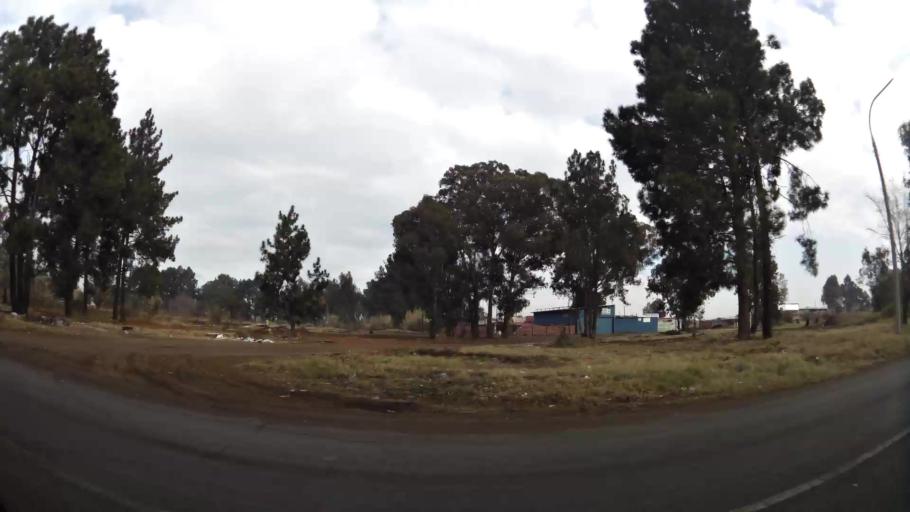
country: ZA
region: Gauteng
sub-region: Sedibeng District Municipality
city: Vanderbijlpark
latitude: -26.6949
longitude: 27.8112
